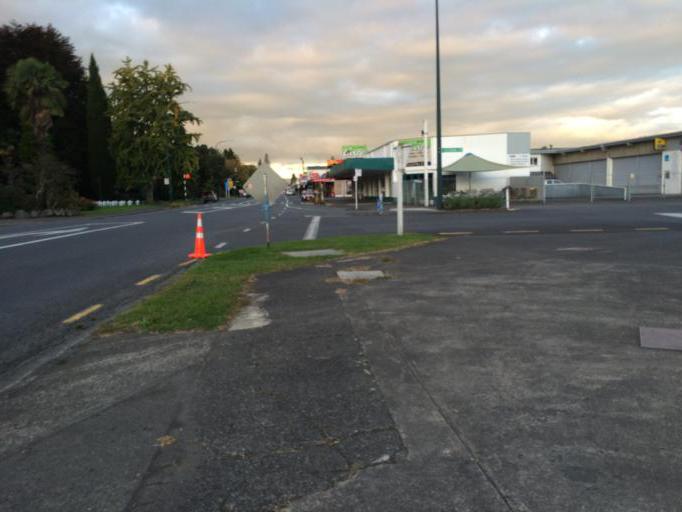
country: NZ
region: Waikato
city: Turangi
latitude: -38.8832
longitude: 175.2588
